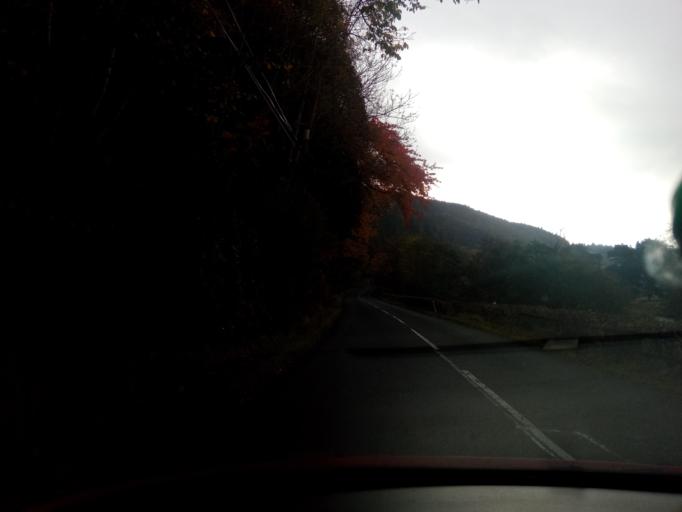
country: GB
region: Scotland
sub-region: The Scottish Borders
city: Selkirk
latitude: 55.6014
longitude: -2.8696
